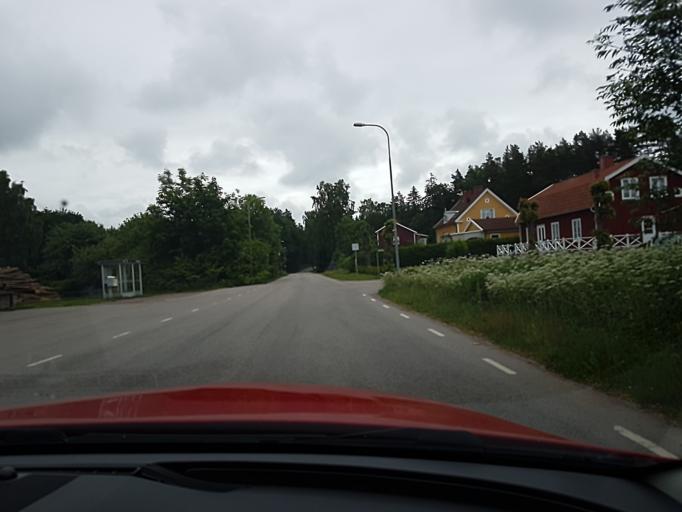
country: SE
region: Vaestra Goetaland
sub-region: Tidaholms Kommun
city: Olofstorp
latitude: 58.3035
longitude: 14.0992
